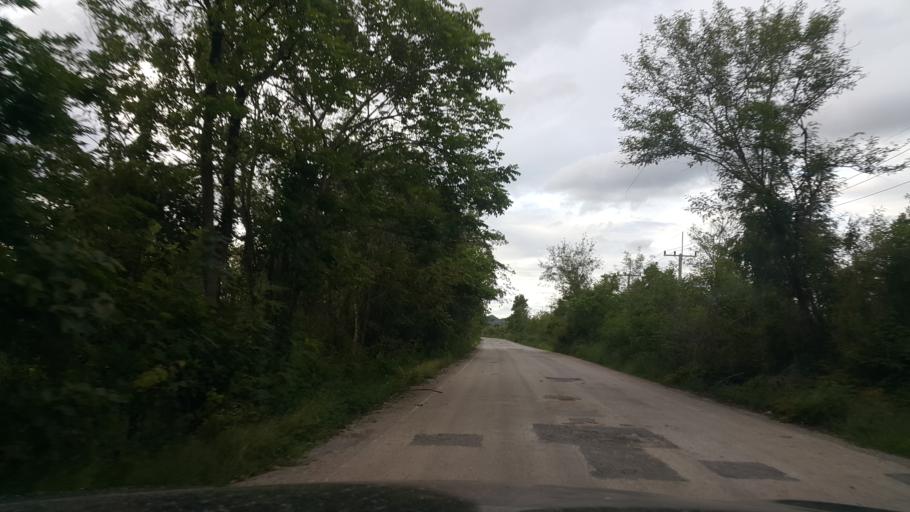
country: TH
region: Sukhothai
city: Thung Saliam
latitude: 17.1712
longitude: 99.5246
